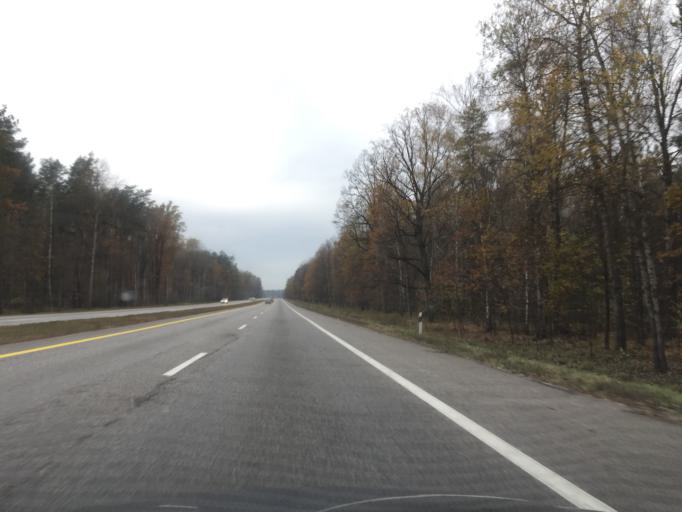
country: BY
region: Gomel
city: Gomel
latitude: 52.3752
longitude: 30.7754
